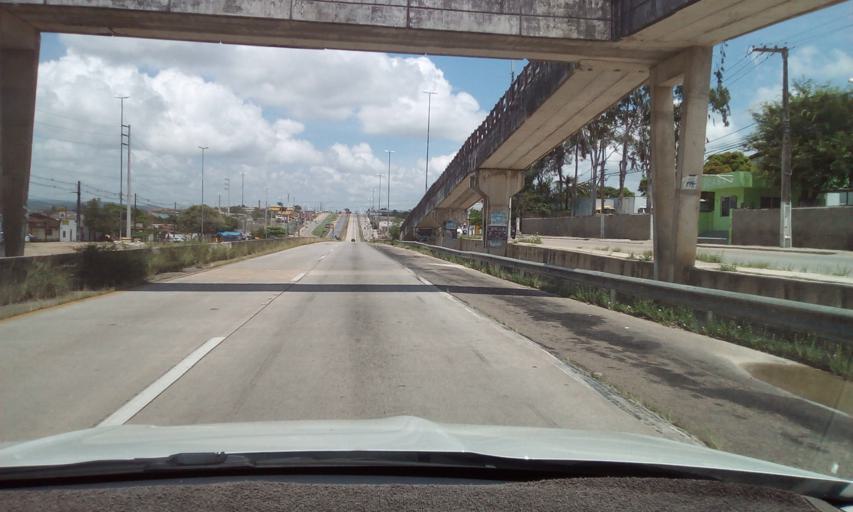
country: BR
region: Pernambuco
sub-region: Gravata
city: Gravata
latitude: -8.1962
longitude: -35.5728
